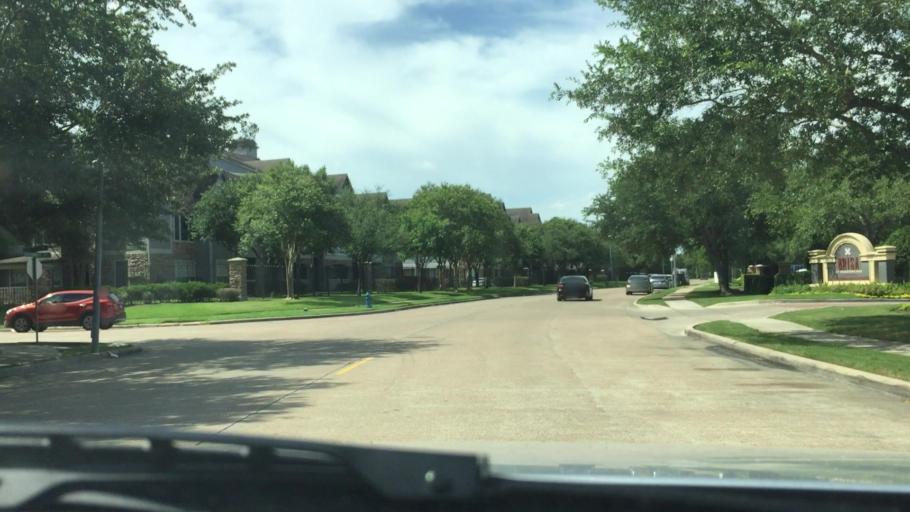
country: US
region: Texas
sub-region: Harris County
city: Bunker Hill Village
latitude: 29.7342
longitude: -95.5982
